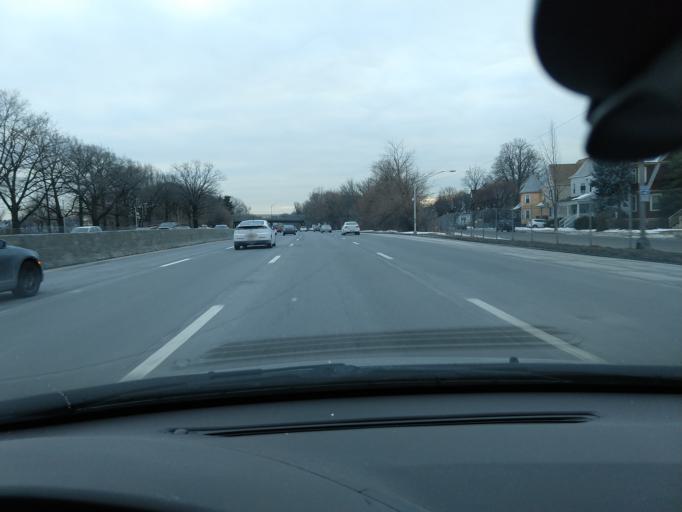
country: US
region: New Jersey
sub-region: Essex County
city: East Orange
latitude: 40.7514
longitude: -74.2119
